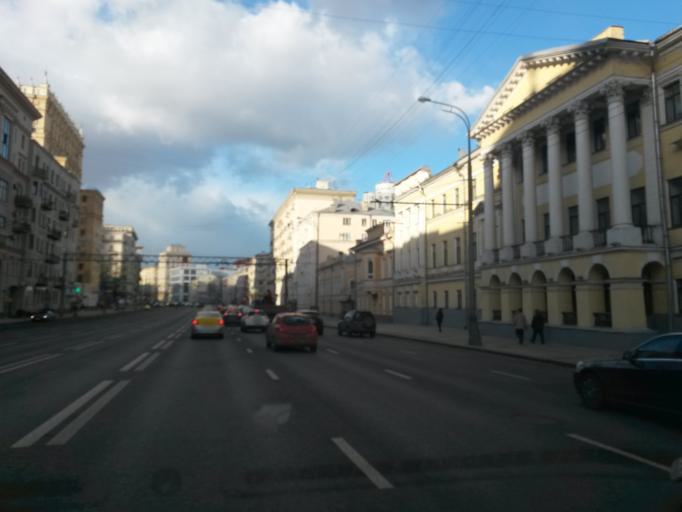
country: RU
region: Moscow
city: Mar'ina Roshcha
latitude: 55.7820
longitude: 37.6340
